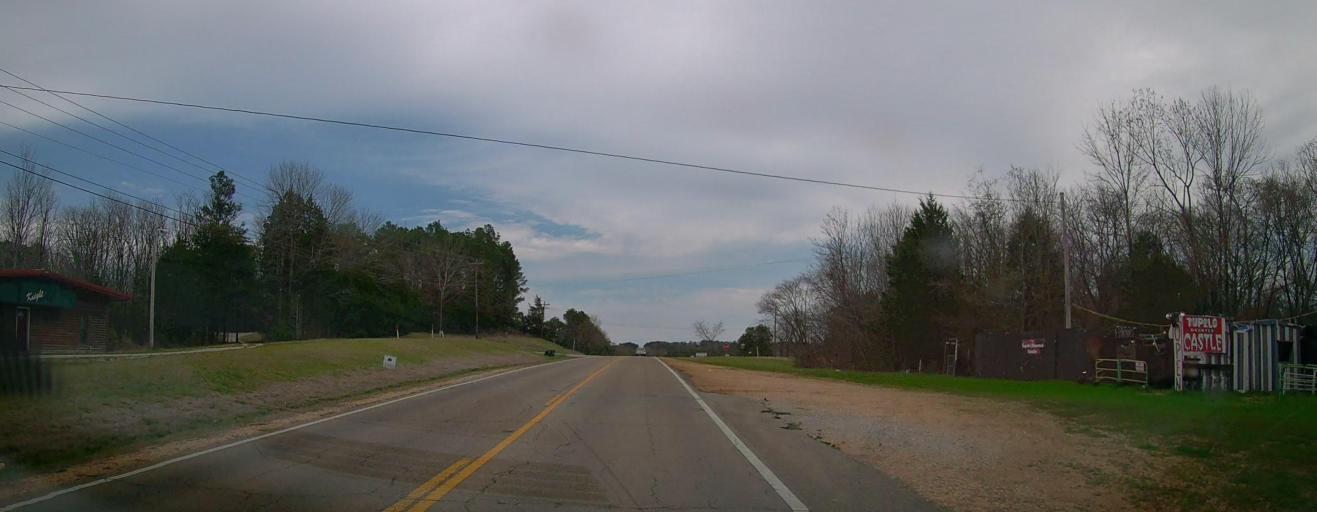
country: US
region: Mississippi
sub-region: Lee County
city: Plantersville
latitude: 34.2660
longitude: -88.6136
